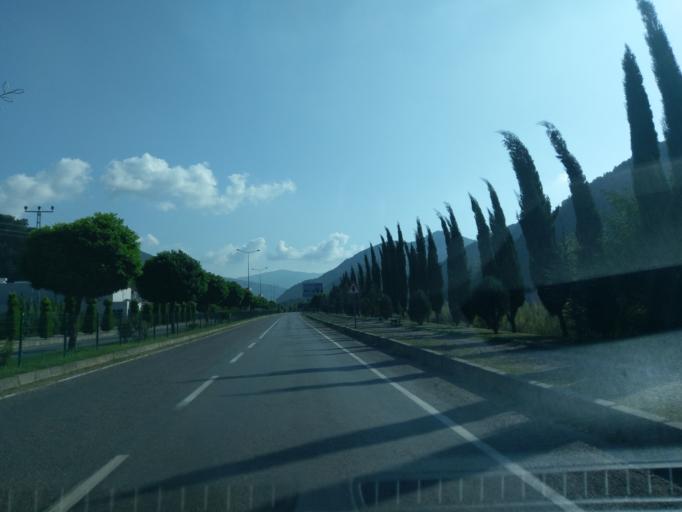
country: TR
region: Sinop
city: Ayancik
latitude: 41.9287
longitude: 34.5842
